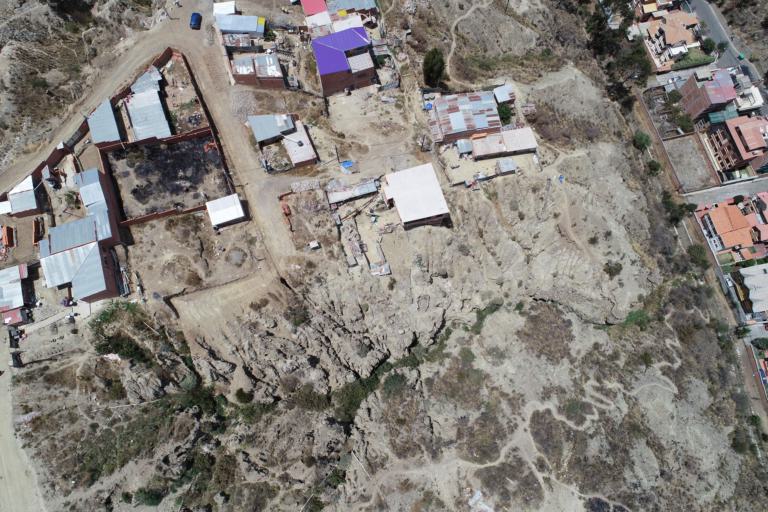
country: BO
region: La Paz
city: La Paz
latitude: -16.5205
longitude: -68.0790
